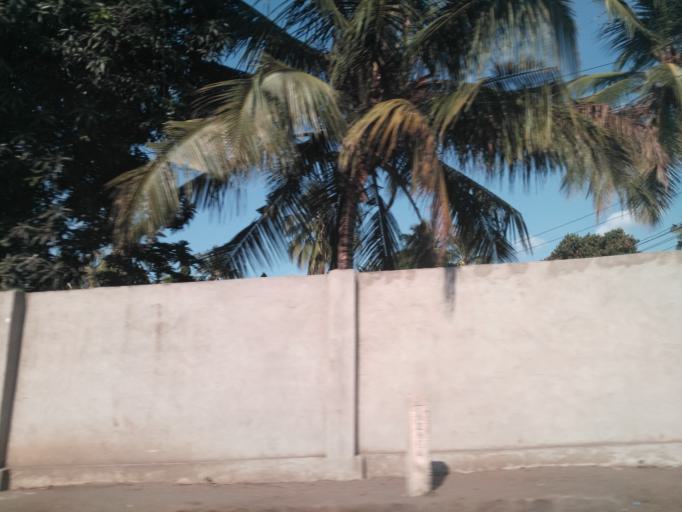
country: TZ
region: Dar es Salaam
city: Dar es Salaam
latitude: -6.8547
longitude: 39.3181
